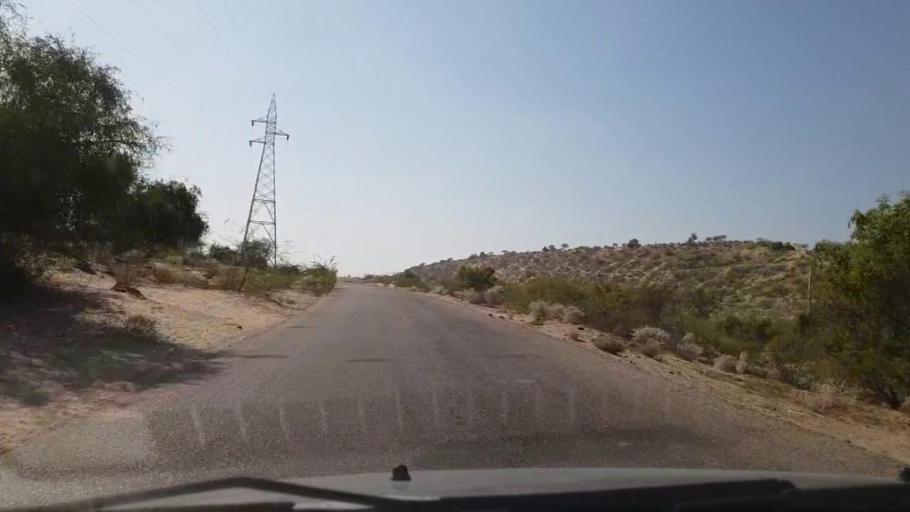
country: PK
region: Sindh
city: Diplo
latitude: 24.5558
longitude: 69.6620
